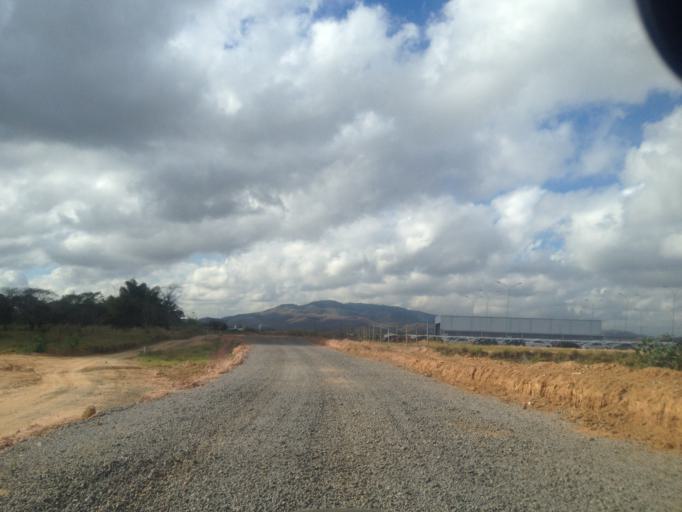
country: BR
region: Rio de Janeiro
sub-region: Resende
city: Resende
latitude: -22.4281
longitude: -44.3805
